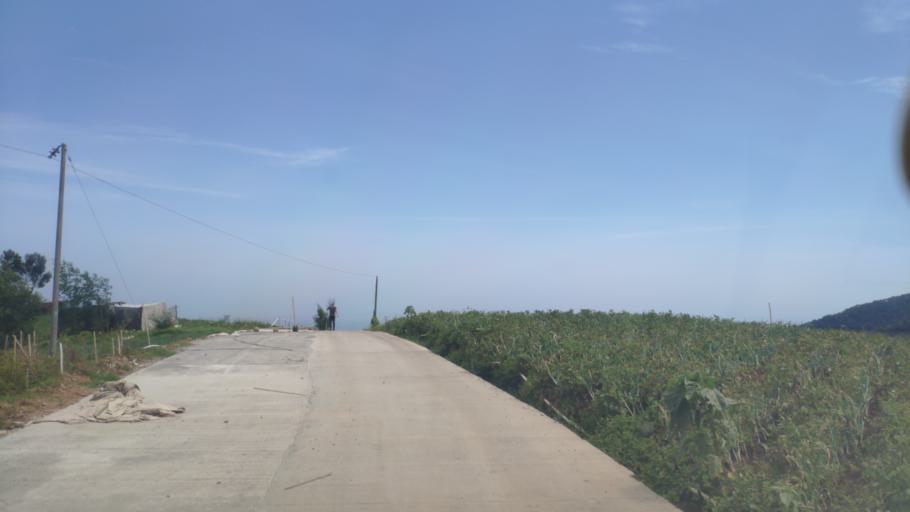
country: ID
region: Central Java
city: Wonosobo
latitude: -7.1786
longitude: 109.8951
